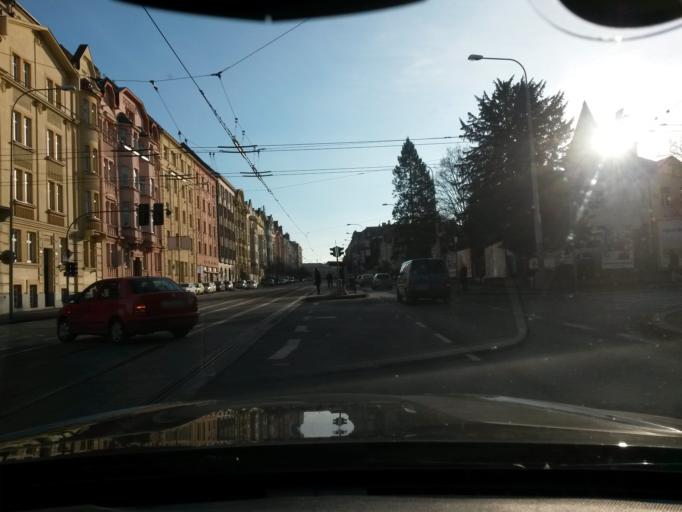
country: CZ
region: Plzensky
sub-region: Okres Plzen-Mesto
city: Pilsen
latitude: 49.7351
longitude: 13.3703
